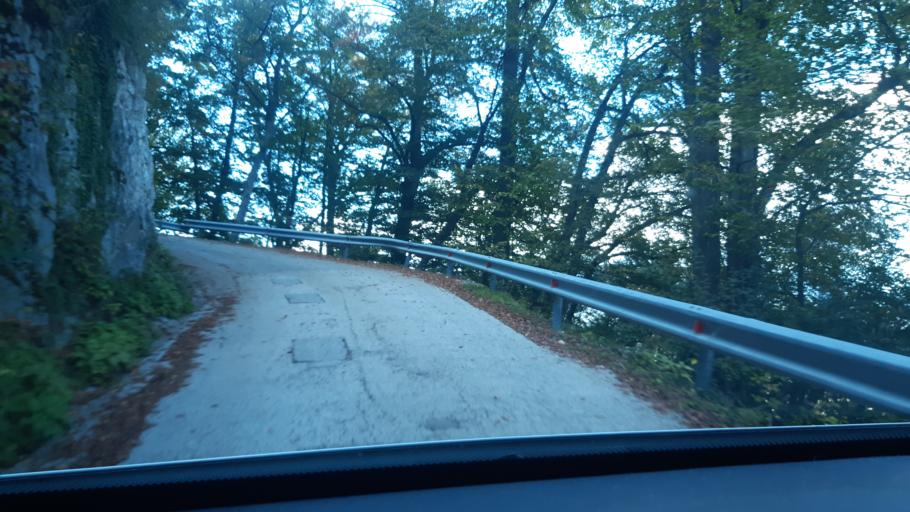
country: SI
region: Kranj
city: Kranj
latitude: 46.2439
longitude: 14.3376
